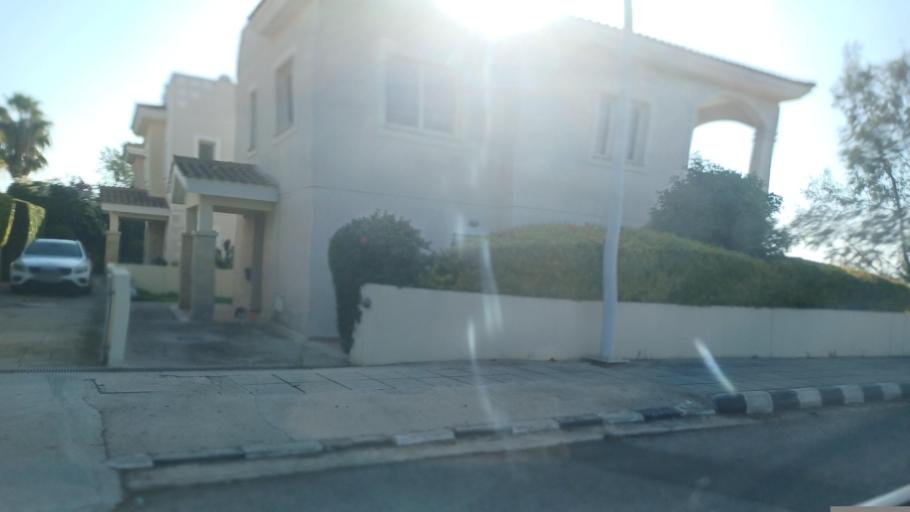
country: CY
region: Pafos
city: Paphos
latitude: 34.7133
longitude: 32.5282
